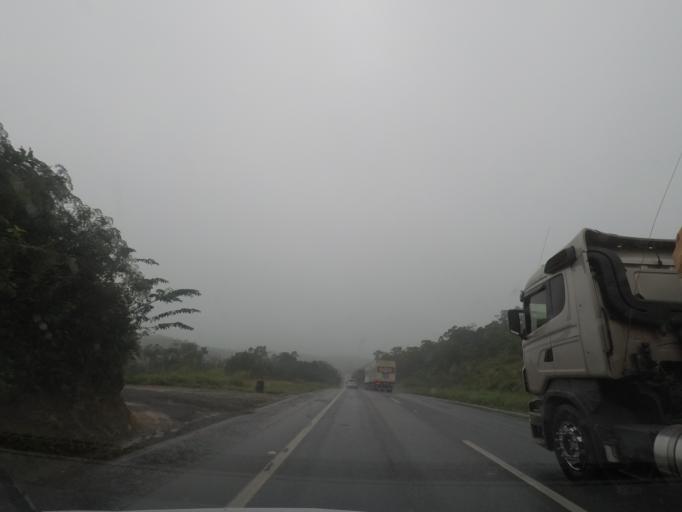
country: BR
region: Parana
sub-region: Campina Grande Do Sul
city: Campina Grande do Sul
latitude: -25.1100
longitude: -48.7961
